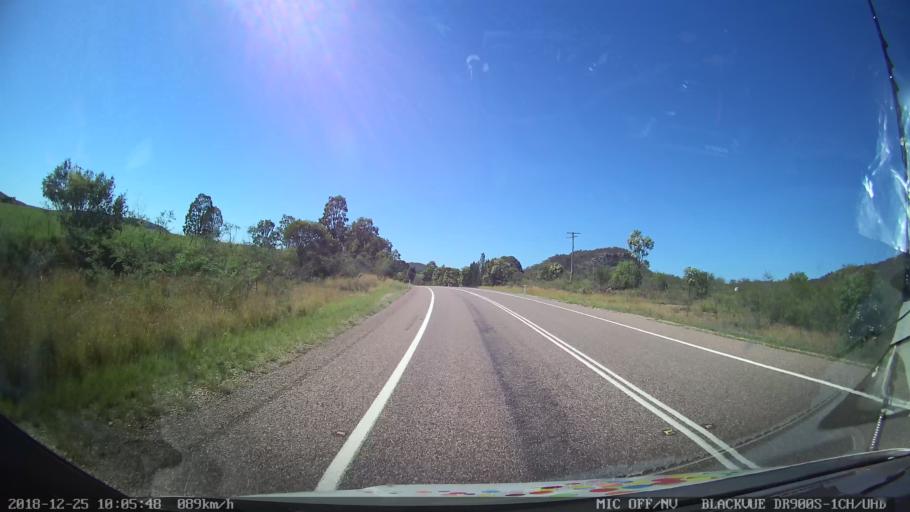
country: AU
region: New South Wales
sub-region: Upper Hunter Shire
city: Merriwa
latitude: -32.2519
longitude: 150.4868
